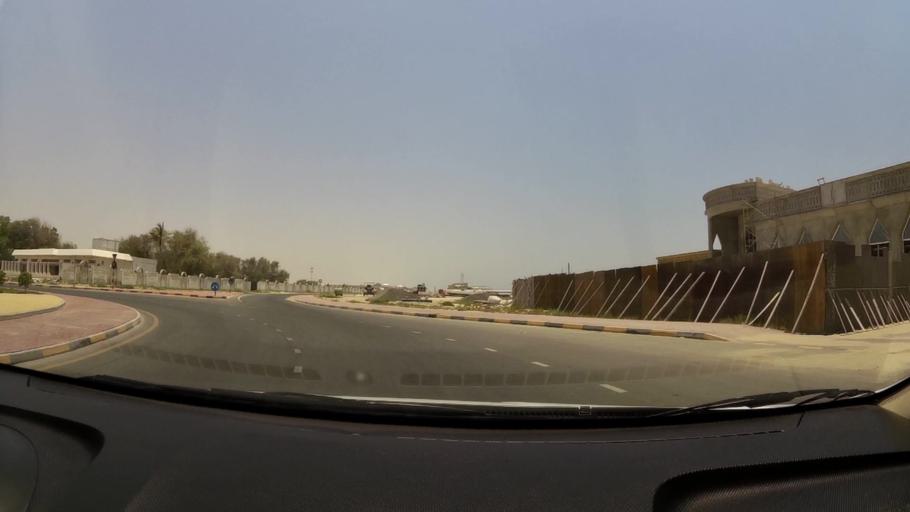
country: AE
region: Umm al Qaywayn
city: Umm al Qaywayn
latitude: 25.5566
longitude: 55.5431
